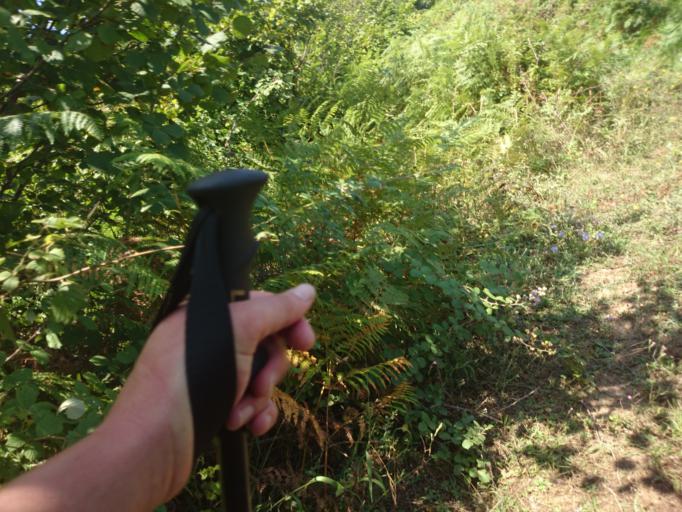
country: AL
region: Diber
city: Peshkopi
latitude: 41.6328
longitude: 20.4098
